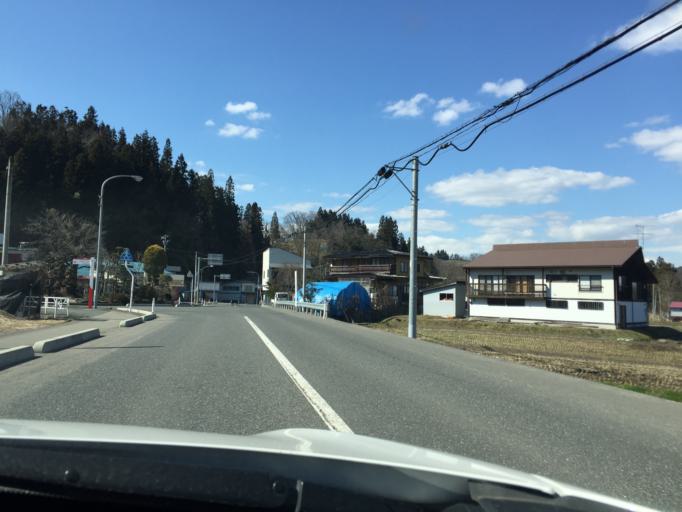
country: JP
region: Yamagata
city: Sagae
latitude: 38.2891
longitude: 140.1229
